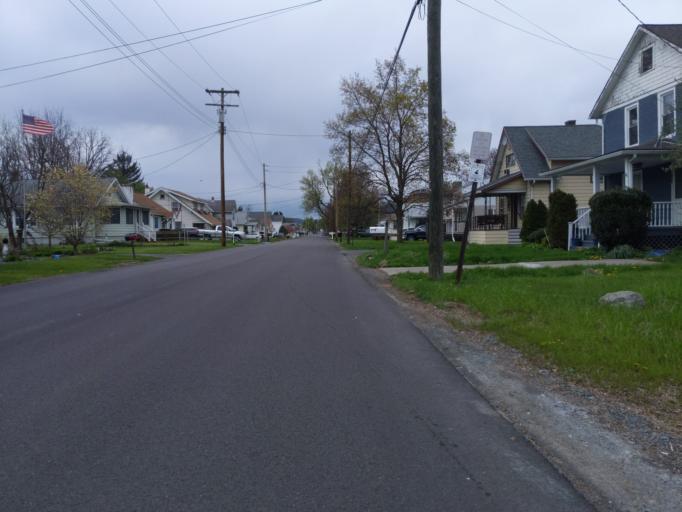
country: US
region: New York
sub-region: Chemung County
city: Southport
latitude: 42.0610
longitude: -76.8111
